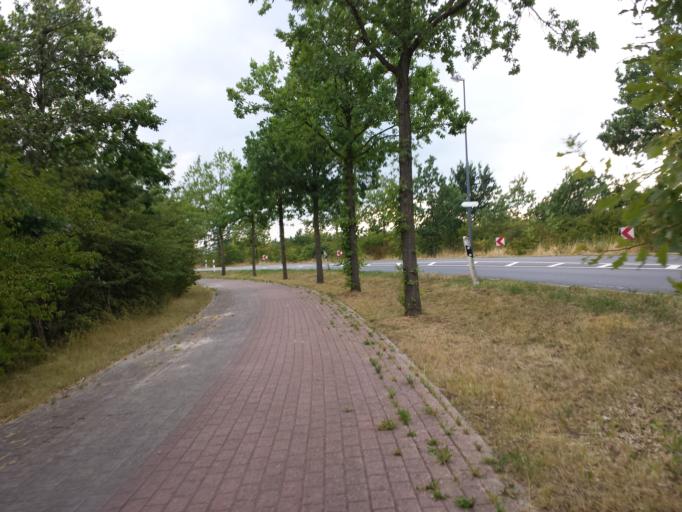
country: DE
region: Lower Saxony
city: Stuhr
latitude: 53.0870
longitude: 8.7307
